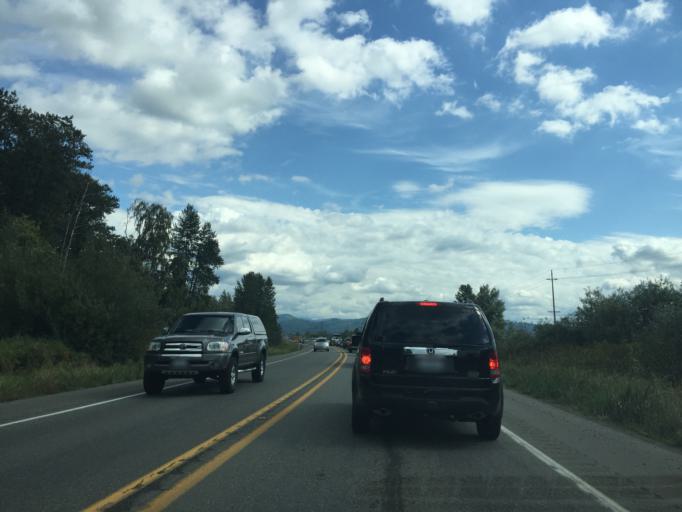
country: US
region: Washington
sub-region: Snohomish County
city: Monroe
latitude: 47.8751
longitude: -122.0143
